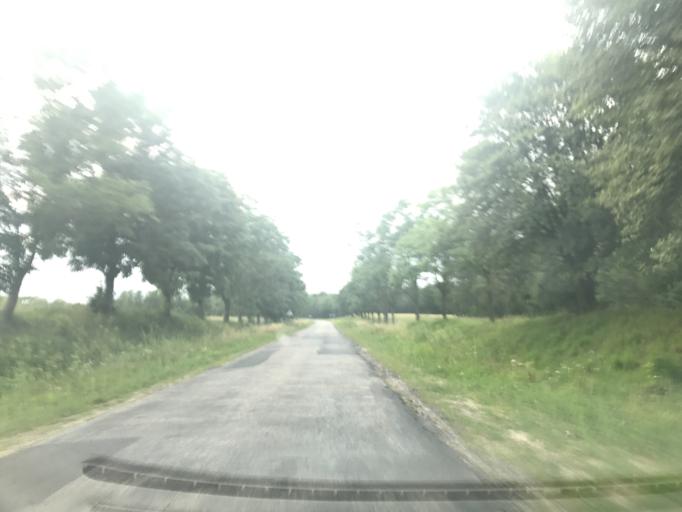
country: PL
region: Kujawsko-Pomorskie
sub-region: Powiat lipnowski
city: Lipno
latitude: 52.7967
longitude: 19.2052
